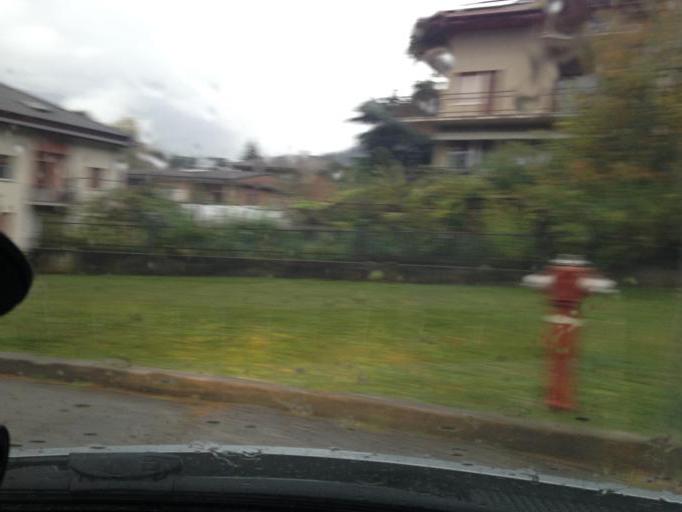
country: IT
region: Trentino-Alto Adige
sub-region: Provincia di Trento
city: Rovereto
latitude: 45.8988
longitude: 11.0456
